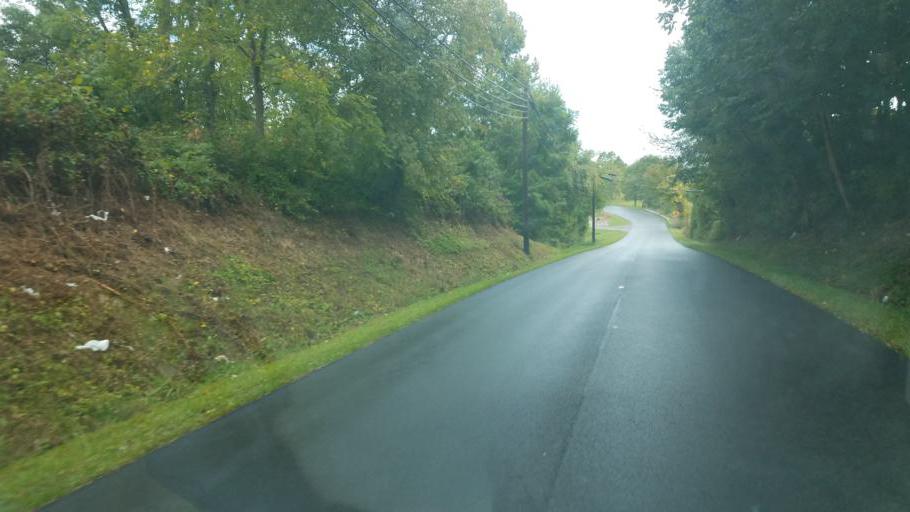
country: US
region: Ohio
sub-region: Scioto County
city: Lucasville
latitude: 38.8805
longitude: -82.9887
